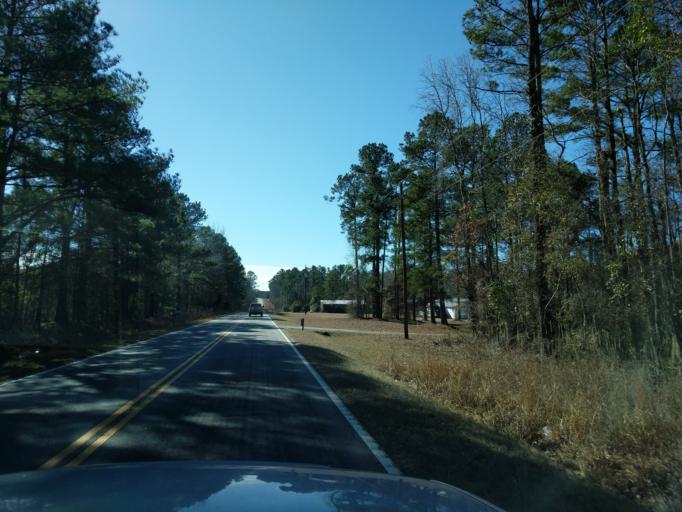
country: US
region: South Carolina
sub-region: Greenwood County
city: Ninety Six
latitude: 34.2107
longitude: -81.8830
